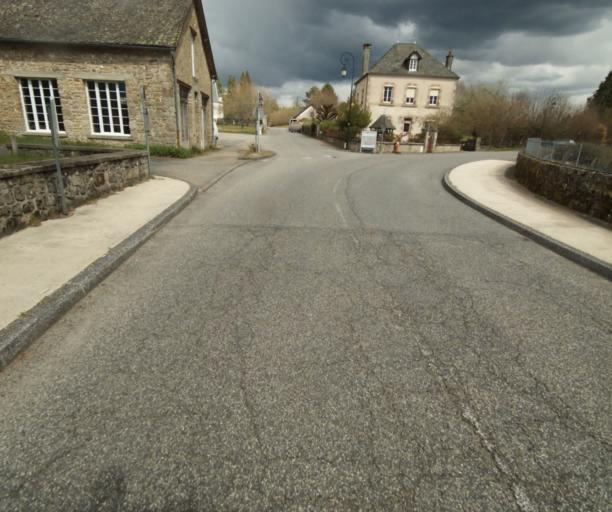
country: FR
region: Limousin
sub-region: Departement de la Correze
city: Correze
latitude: 45.2791
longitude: 1.9751
